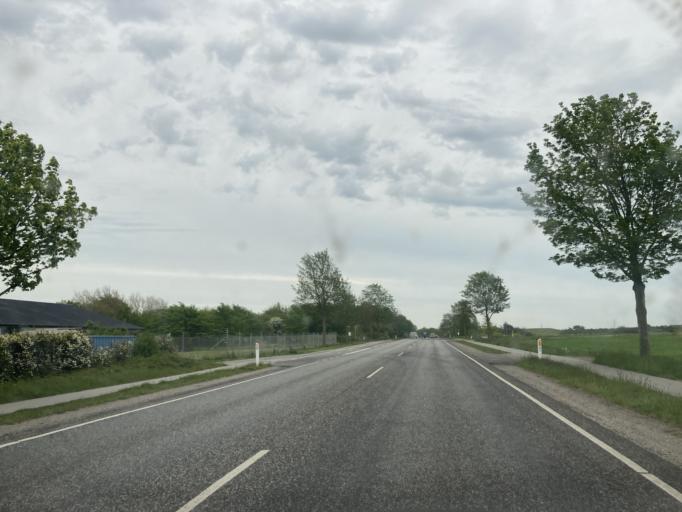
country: DK
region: Zealand
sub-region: Roskilde Kommune
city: Svogerslev
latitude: 55.6316
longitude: 12.0077
